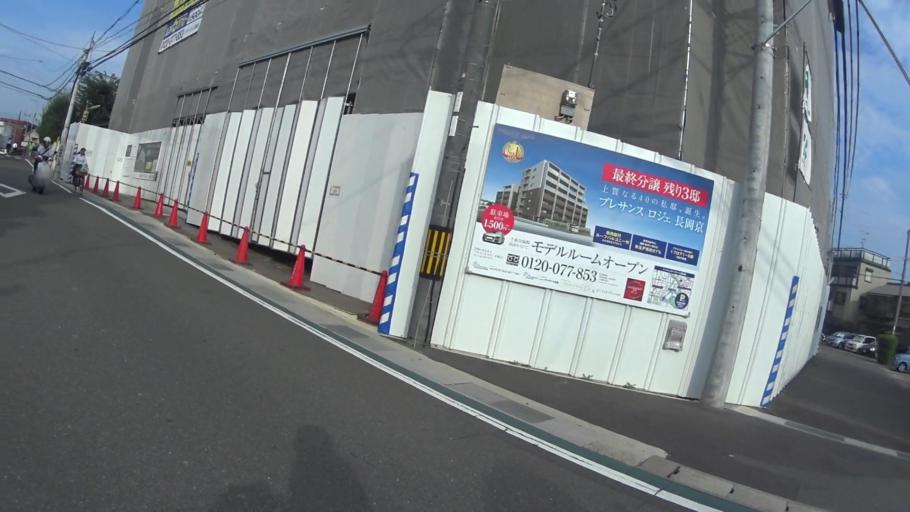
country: JP
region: Kyoto
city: Muko
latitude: 34.9271
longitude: 135.7054
